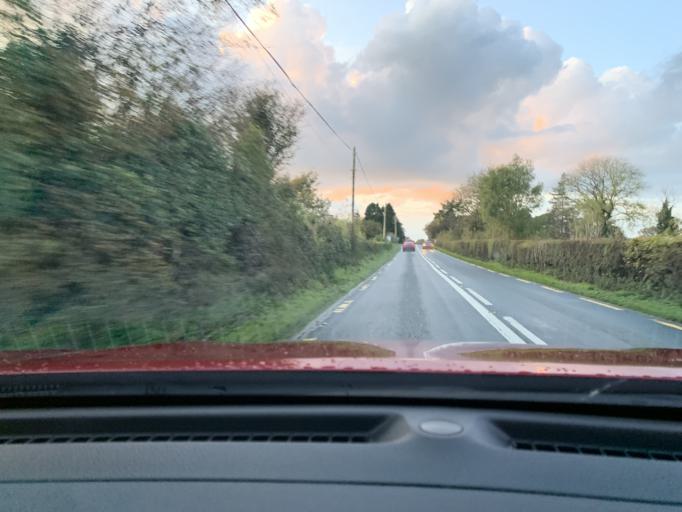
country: IE
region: Connaught
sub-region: Sligo
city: Ballymote
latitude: 54.1054
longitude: -8.4113
